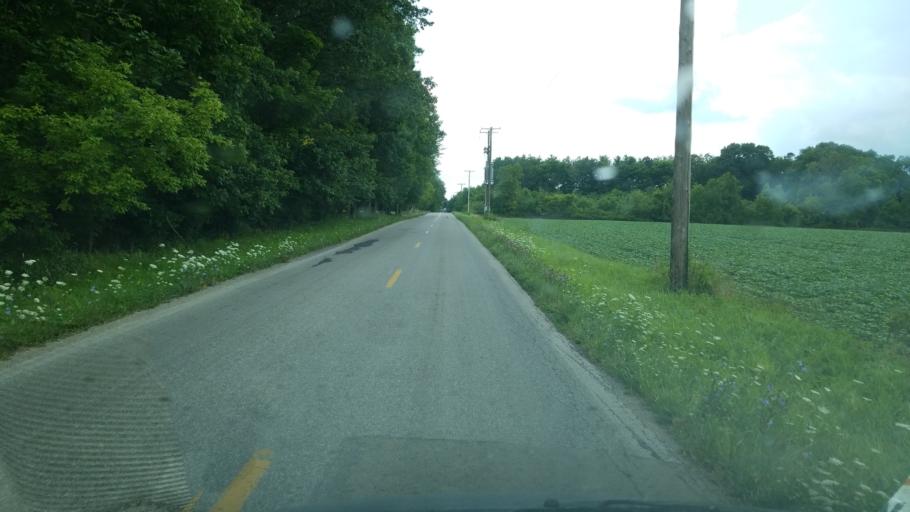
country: US
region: Ohio
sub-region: Morrow County
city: Cardington
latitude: 40.4694
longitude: -82.9457
